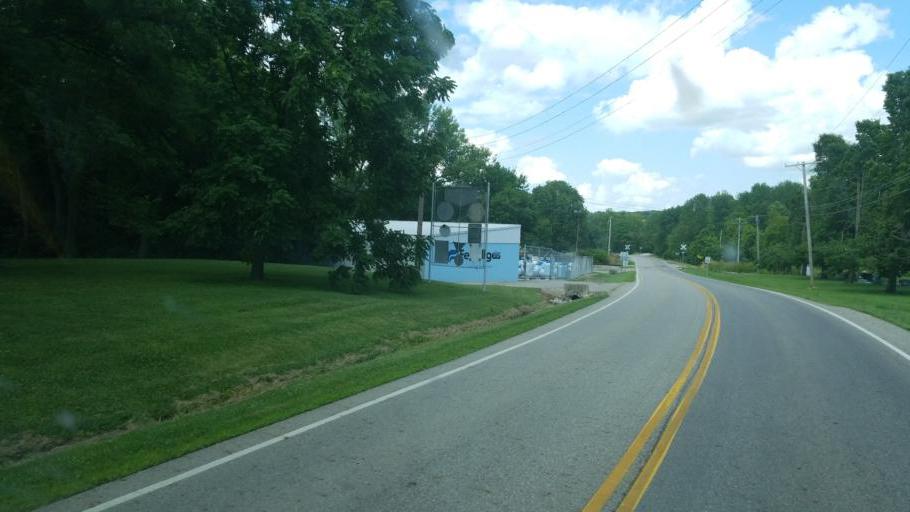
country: US
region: Ohio
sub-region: Highland County
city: Greenfield
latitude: 39.3607
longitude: -83.3835
